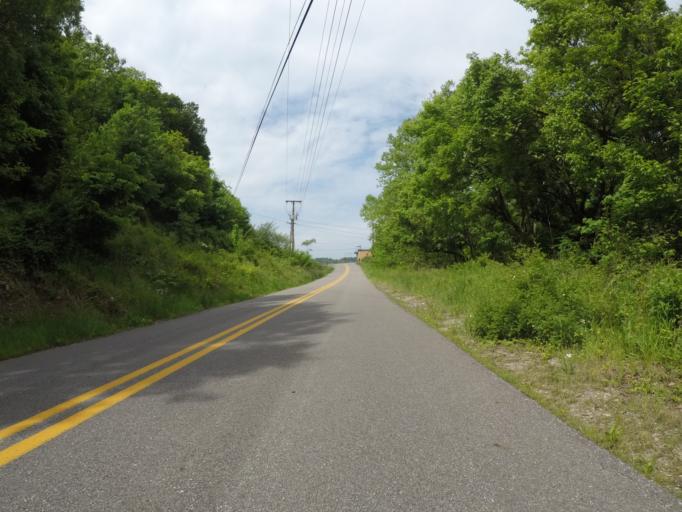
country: US
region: West Virginia
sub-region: Wayne County
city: Kenova
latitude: 38.3356
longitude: -82.5788
